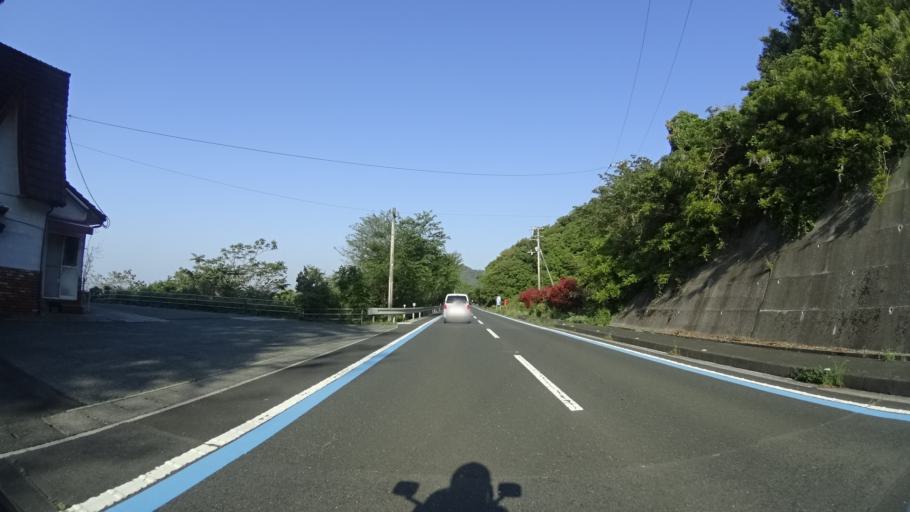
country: JP
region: Ehime
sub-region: Nishiuwa-gun
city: Ikata-cho
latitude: 33.4316
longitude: 132.2265
